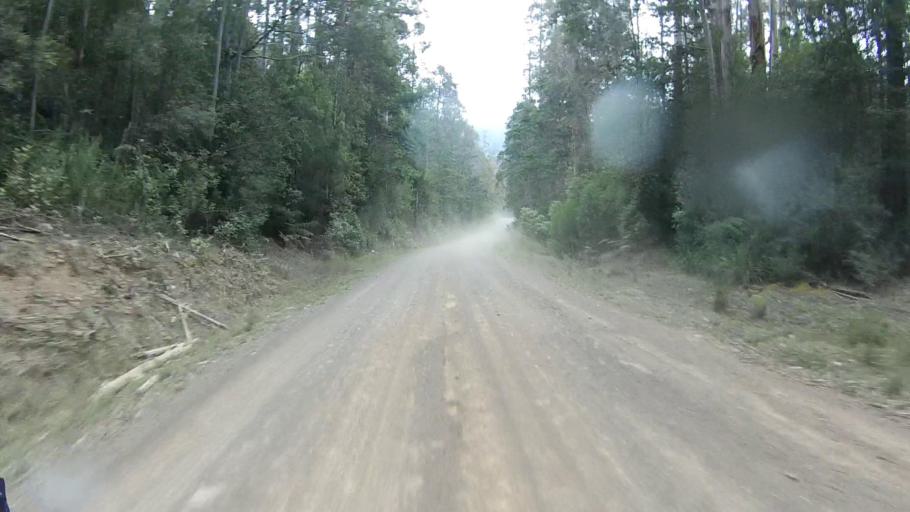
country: AU
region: Tasmania
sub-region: Sorell
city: Sorell
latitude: -42.7082
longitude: 147.8406
